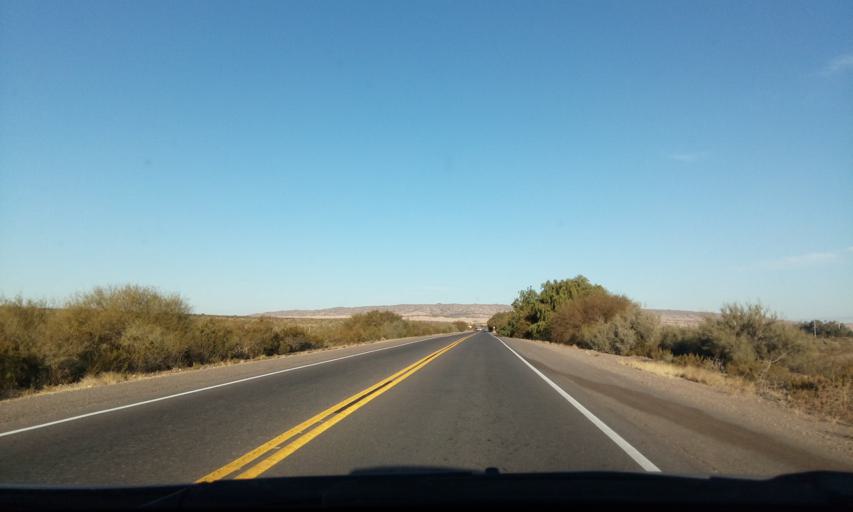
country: AR
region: San Juan
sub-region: Departamento de Rivadavia
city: Rivadavia
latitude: -31.4325
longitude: -68.6632
